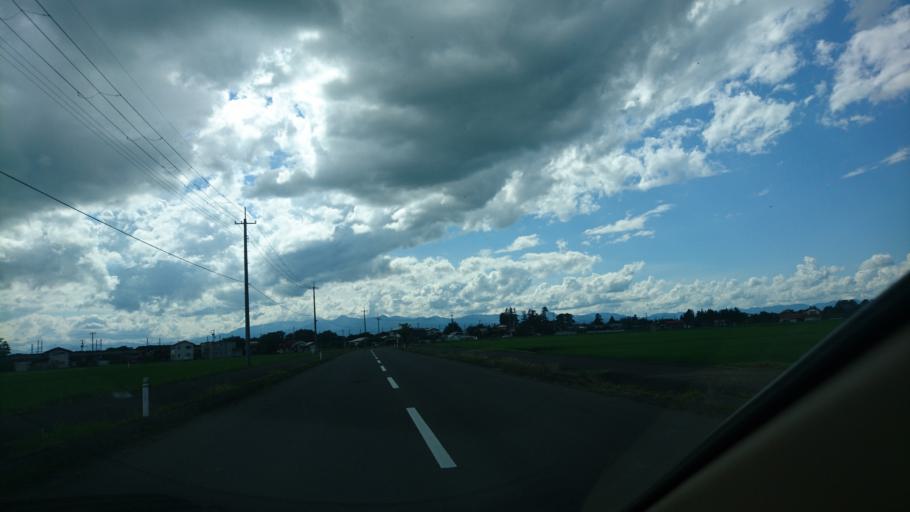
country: JP
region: Iwate
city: Mizusawa
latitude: 39.1925
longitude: 141.1663
